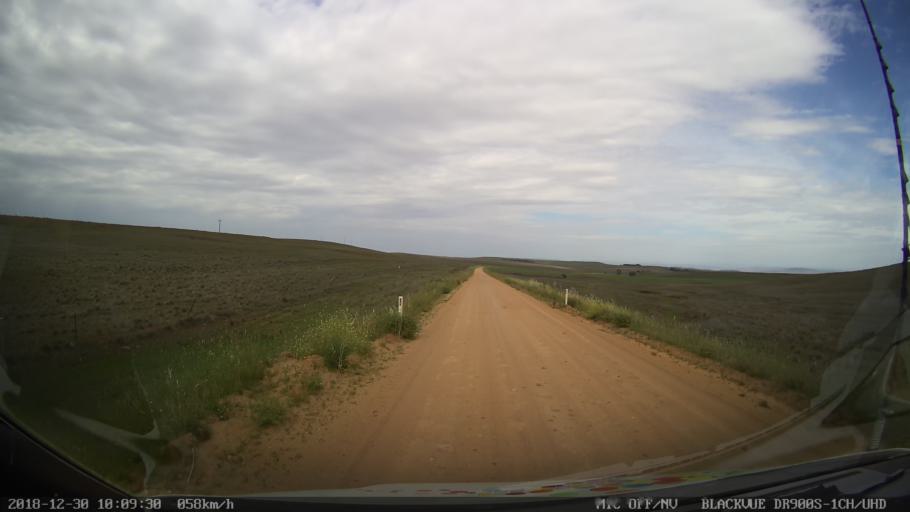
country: AU
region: New South Wales
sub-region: Cooma-Monaro
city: Cooma
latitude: -36.5485
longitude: 149.1049
